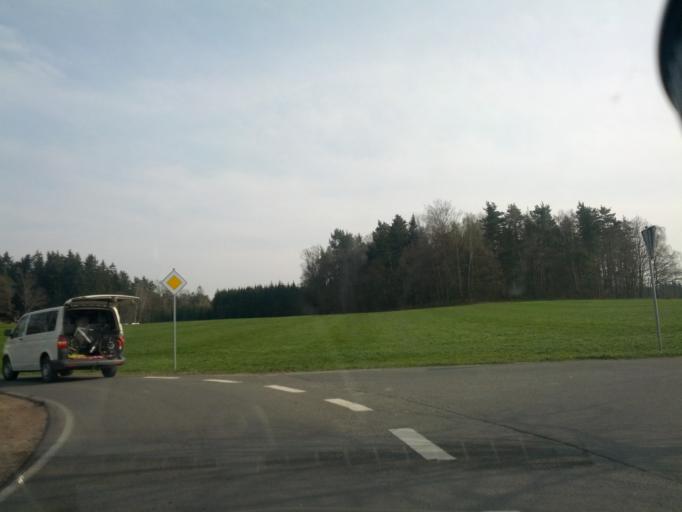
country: DE
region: Saxony
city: Kirchberg
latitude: 50.5808
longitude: 12.5150
